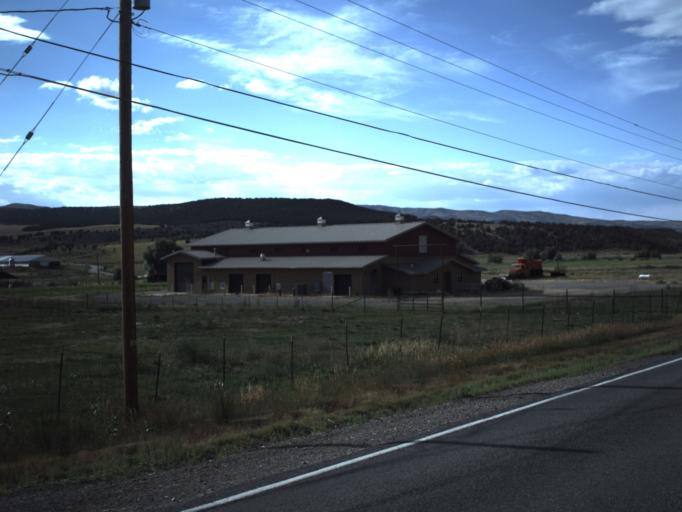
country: US
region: Utah
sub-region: Sanpete County
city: Fairview
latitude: 39.6060
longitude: -111.4447
